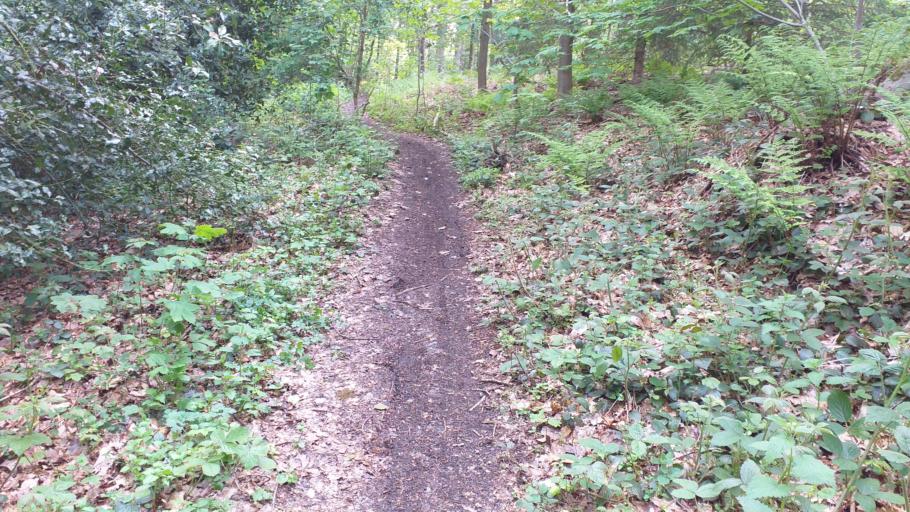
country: DE
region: North Rhine-Westphalia
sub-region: Regierungsbezirk Koln
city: Aachen
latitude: 50.7330
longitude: 6.0736
